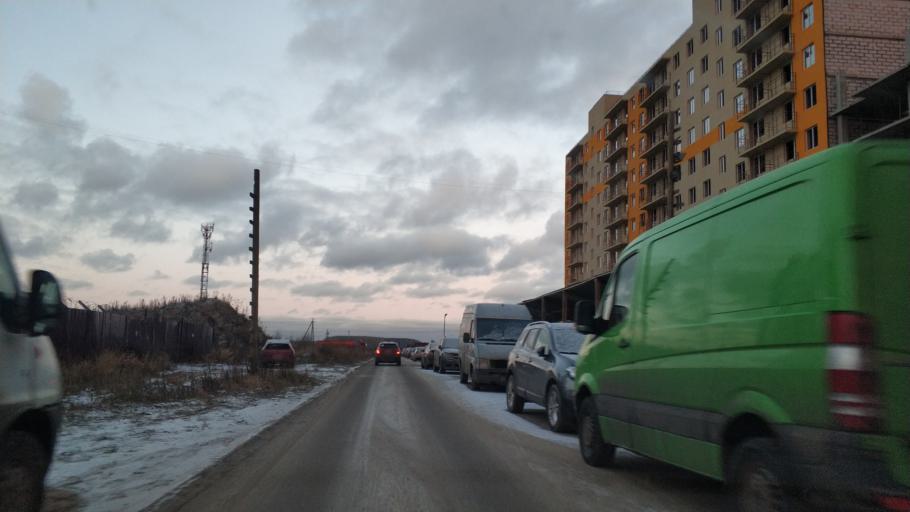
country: RU
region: St.-Petersburg
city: Pontonnyy
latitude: 59.7994
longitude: 30.6328
